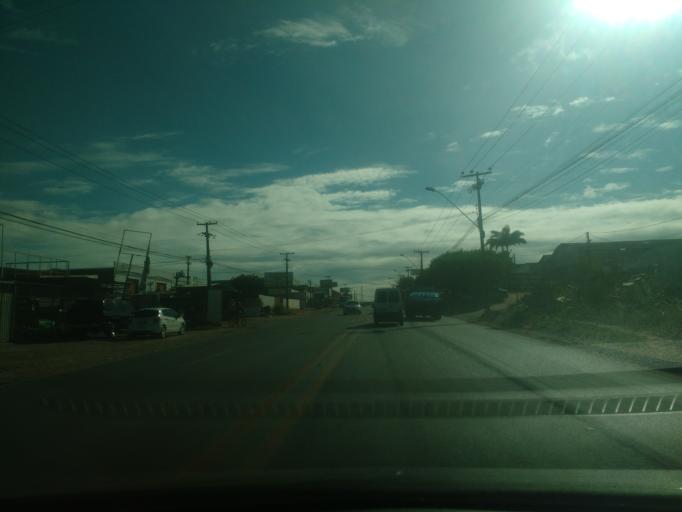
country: BR
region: Alagoas
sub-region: Satuba
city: Satuba
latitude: -9.5628
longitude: -35.7707
